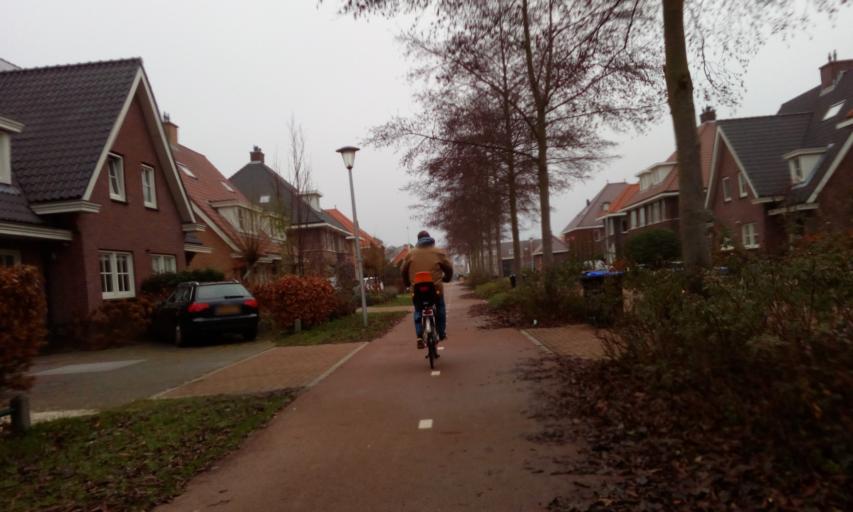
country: NL
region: South Holland
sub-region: Gemeente Lansingerland
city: Berkel en Rodenrijs
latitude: 51.9877
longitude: 4.4577
